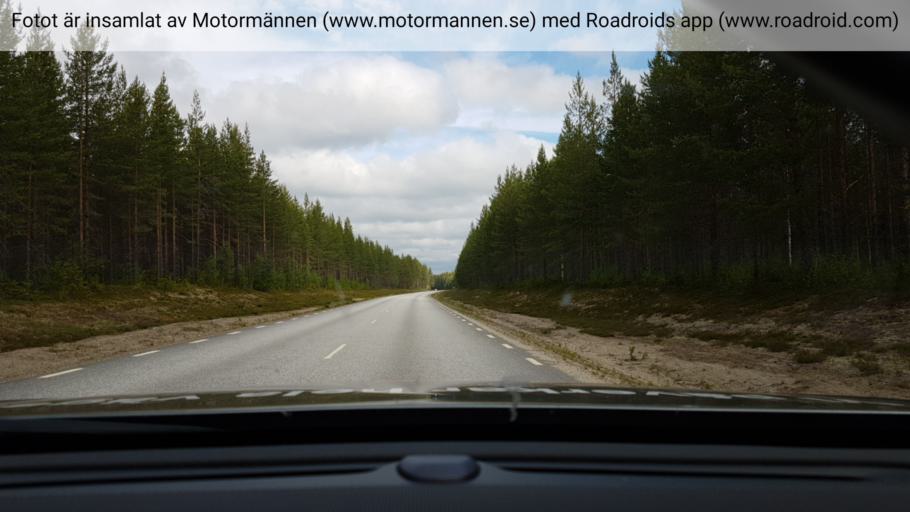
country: SE
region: Vaesterbotten
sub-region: Vindelns Kommun
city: Vindeln
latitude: 64.3657
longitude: 19.4346
